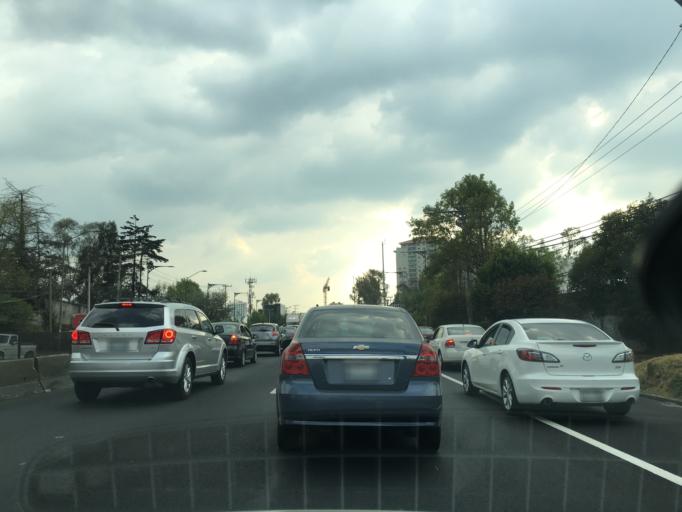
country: MX
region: Mexico City
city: Col. Bosques de las Lomas
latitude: 19.3670
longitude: -99.2719
